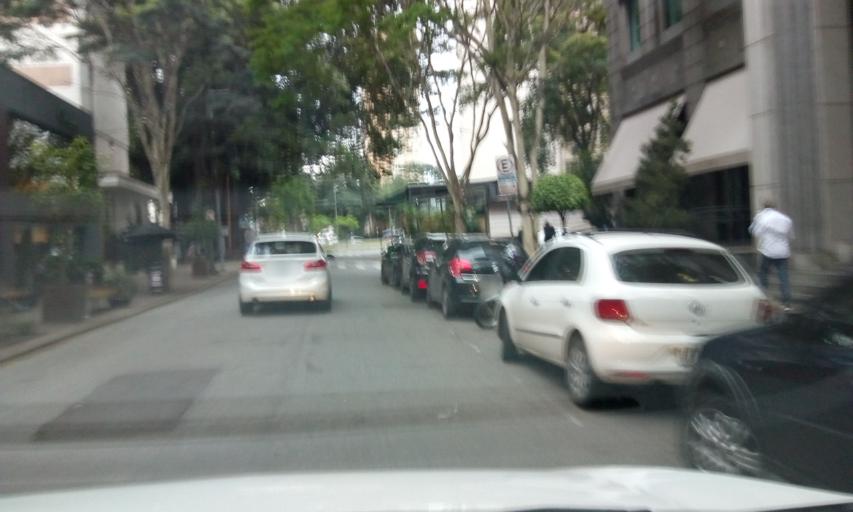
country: BR
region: Sao Paulo
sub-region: Sao Paulo
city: Sao Paulo
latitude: -23.5812
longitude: -46.6829
